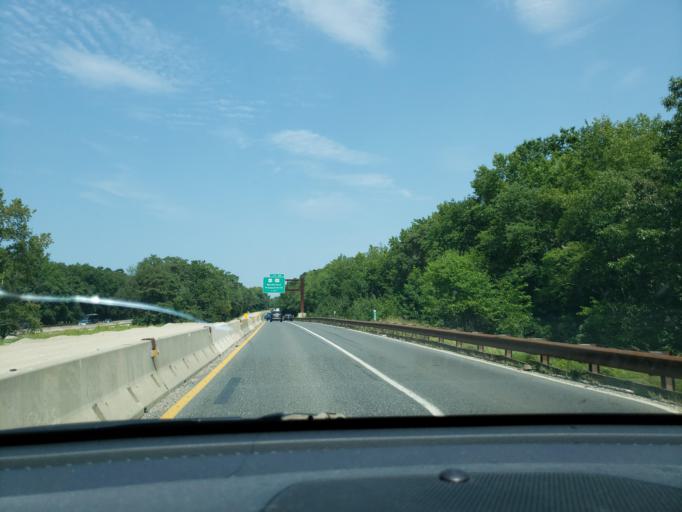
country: US
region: New Jersey
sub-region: Atlantic County
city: Northfield
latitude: 39.3800
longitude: -74.5782
